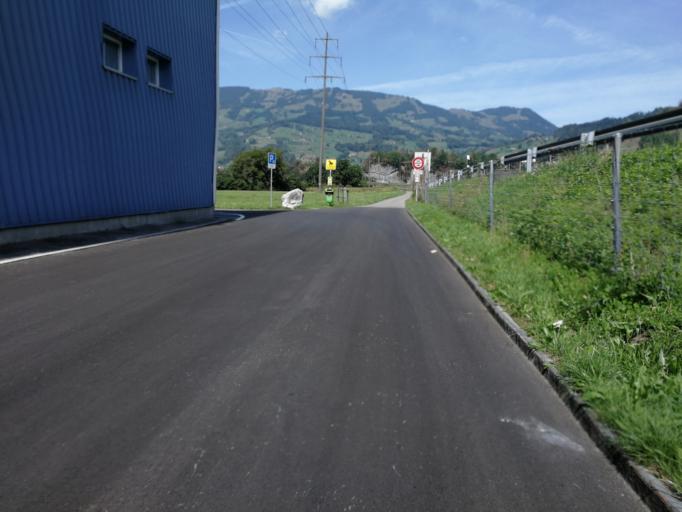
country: CH
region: Schwyz
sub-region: Bezirk Schwyz
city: Steinen
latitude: 47.0314
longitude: 8.6234
